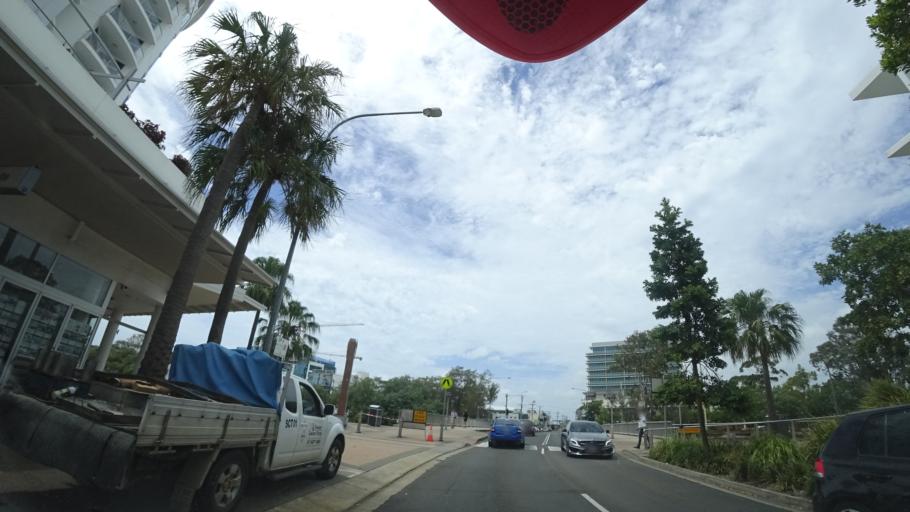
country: AU
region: Queensland
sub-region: Sunshine Coast
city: Mooloolaba
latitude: -26.6533
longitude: 153.0932
